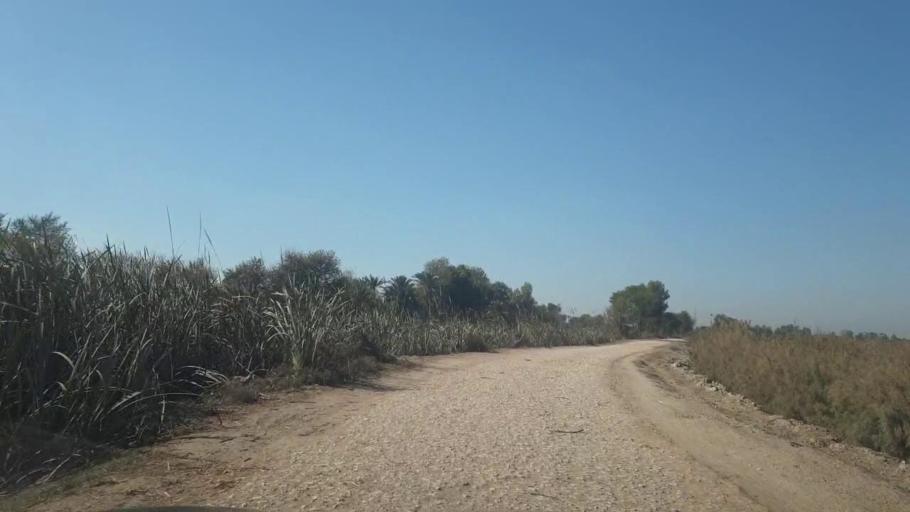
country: PK
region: Sindh
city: Adilpur
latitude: 27.8918
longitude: 69.2843
